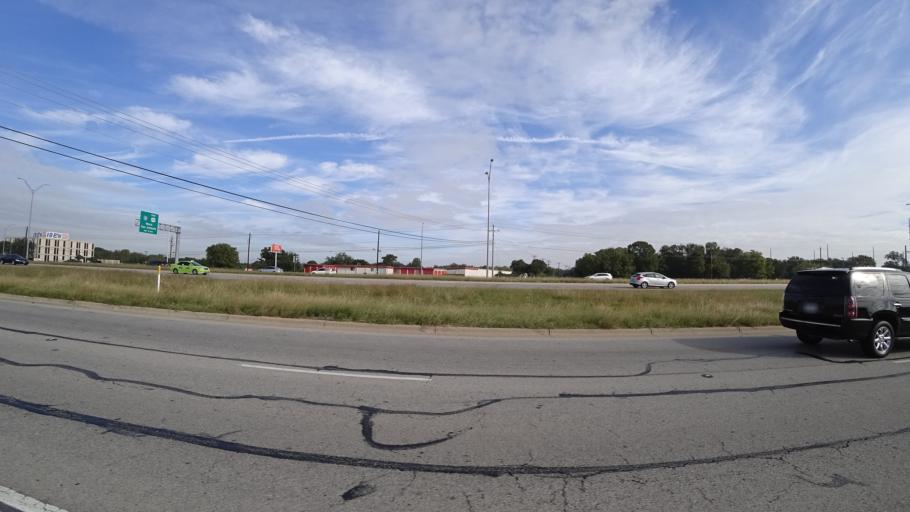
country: US
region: Texas
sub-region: Travis County
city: Austin
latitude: 30.2136
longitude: -97.7264
